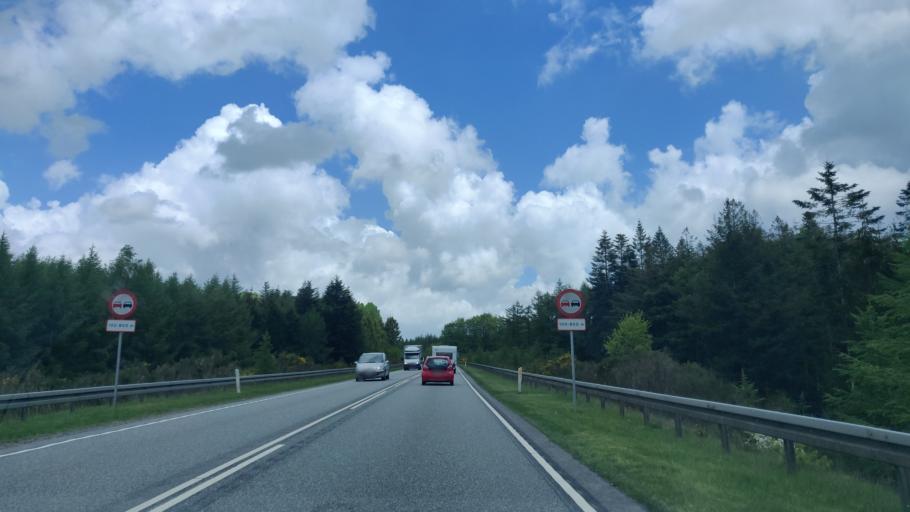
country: DK
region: Central Jutland
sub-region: Hedensted Kommune
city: Torring
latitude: 55.9575
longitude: 9.4004
